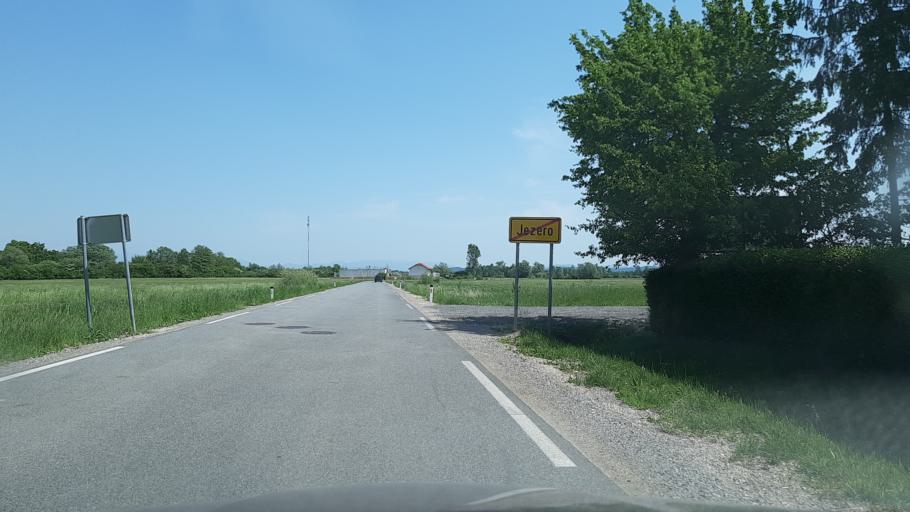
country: SI
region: Brezovica
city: Vnanje Gorice
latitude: 45.9789
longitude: 14.4266
